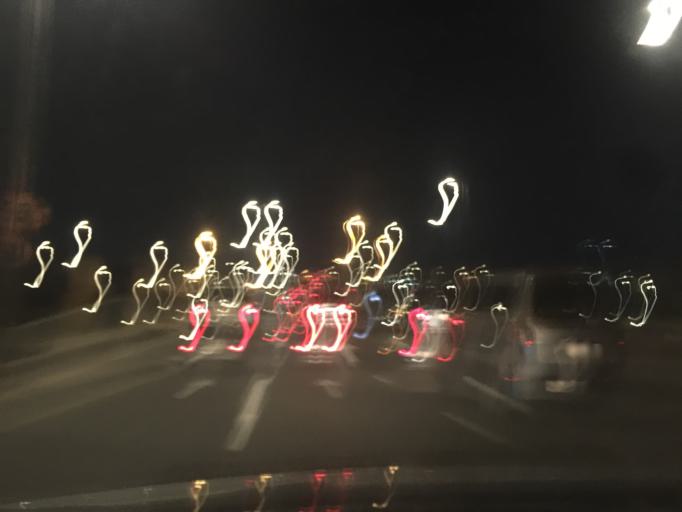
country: JO
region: Amman
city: Wadi as Sir
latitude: 31.9420
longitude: 35.8492
